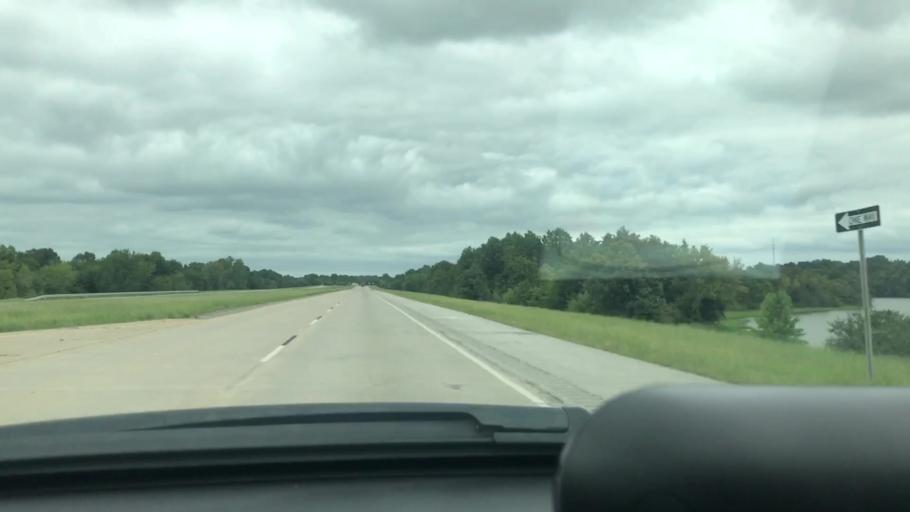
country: US
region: Oklahoma
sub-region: Wagoner County
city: Wagoner
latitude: 35.9004
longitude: -95.4026
